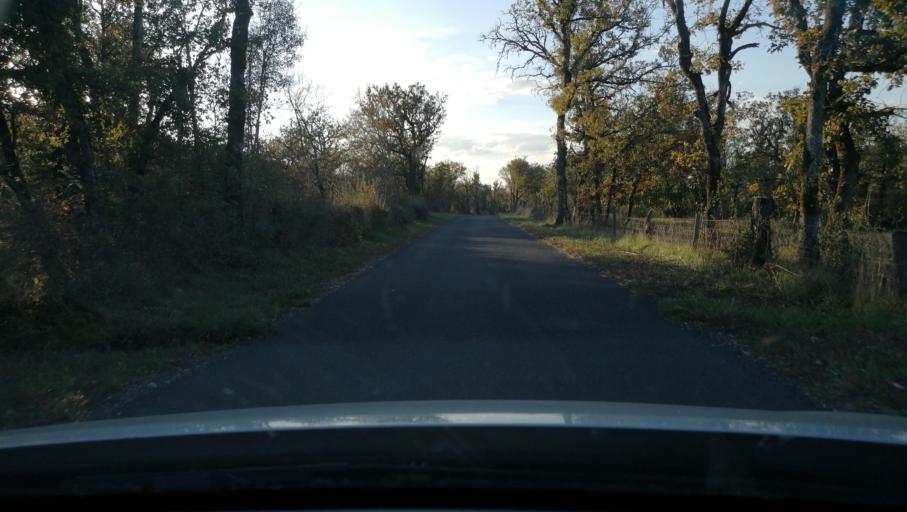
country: FR
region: Midi-Pyrenees
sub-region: Departement du Lot
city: Vayrac
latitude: 44.8694
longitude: 1.6606
